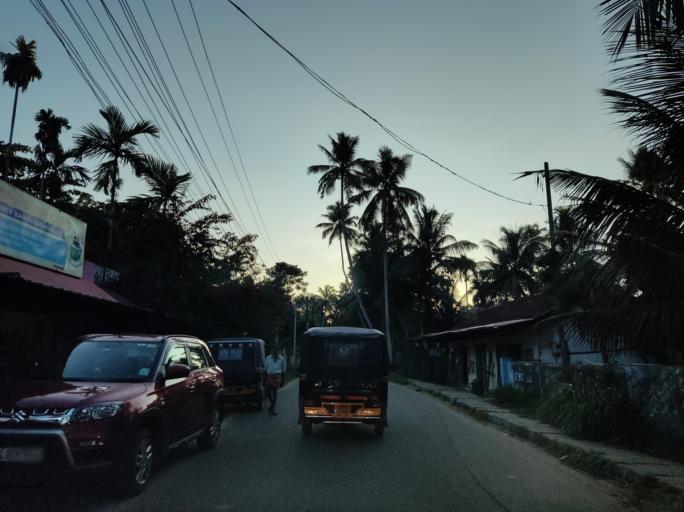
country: IN
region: Kerala
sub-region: Alappuzha
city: Vayalar
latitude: 9.7061
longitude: 76.3004
